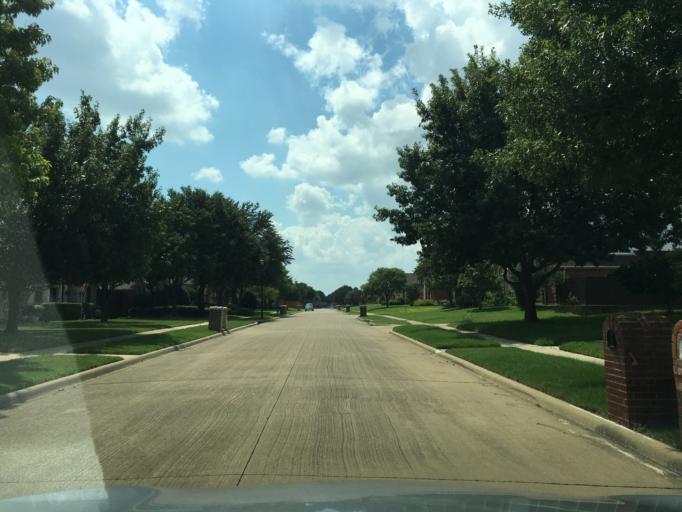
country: US
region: Texas
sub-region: Dallas County
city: Garland
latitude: 32.9425
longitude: -96.6473
